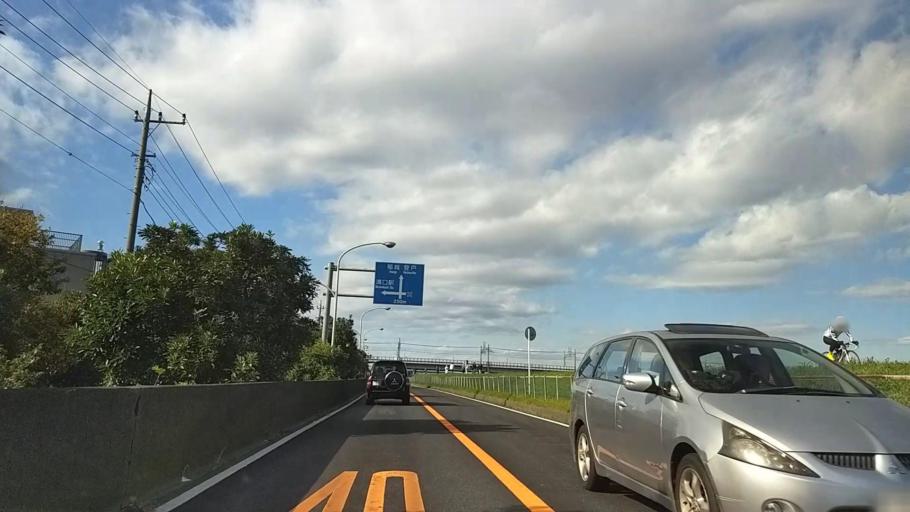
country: JP
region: Tokyo
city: Chofugaoka
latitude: 35.6064
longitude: 139.6261
